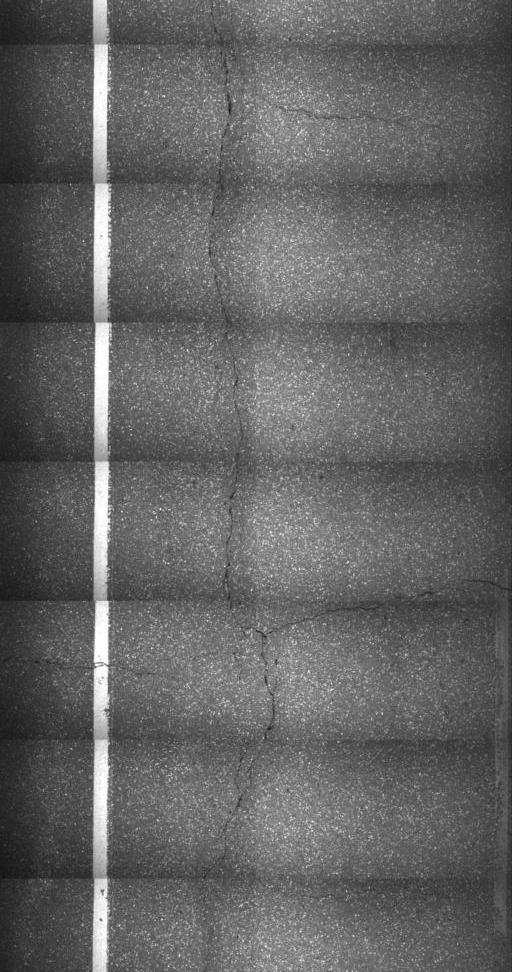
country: US
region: Vermont
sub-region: Caledonia County
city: Hardwick
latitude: 44.6562
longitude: -72.4041
